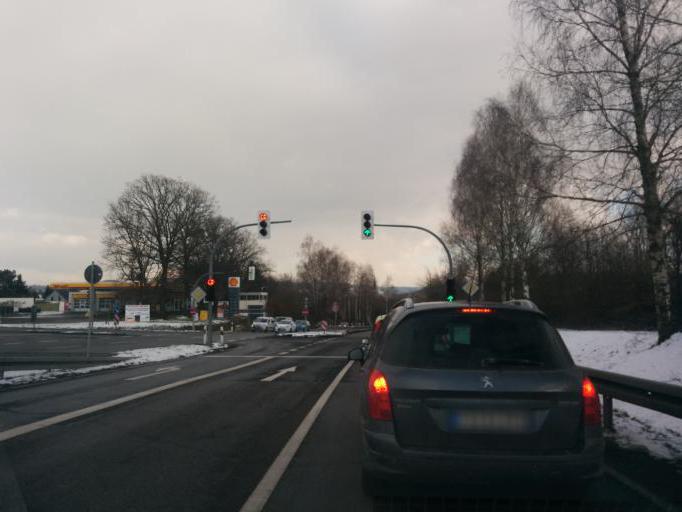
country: DE
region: Saxony
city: Niederwiesa
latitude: 50.8622
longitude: 13.0073
